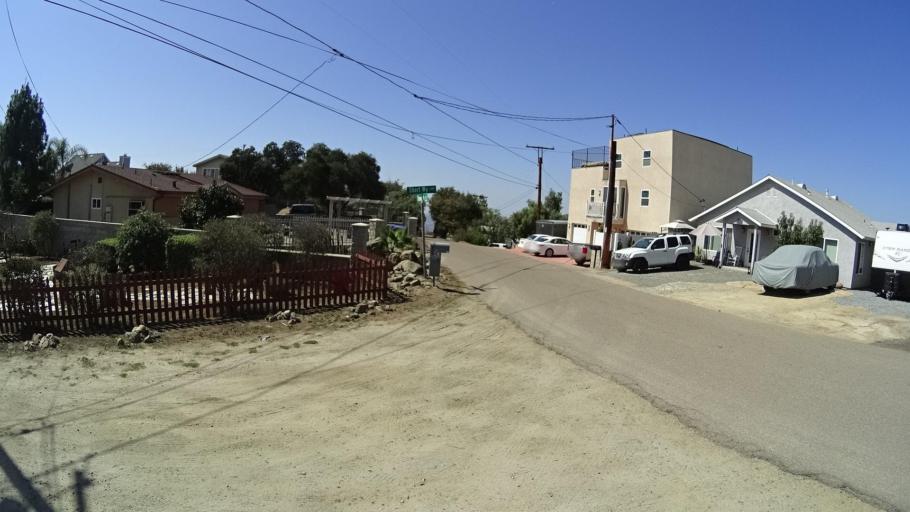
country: US
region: California
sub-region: San Diego County
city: Crest
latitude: 32.8099
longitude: -116.8659
